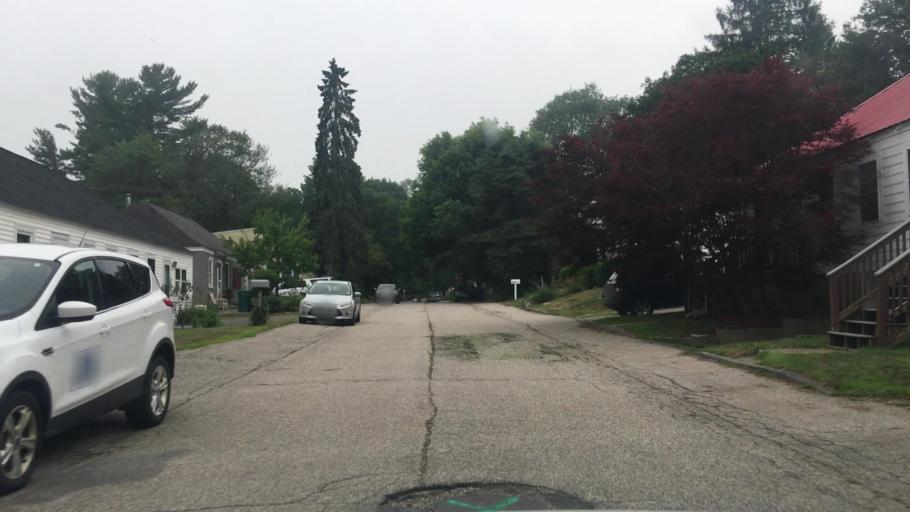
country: US
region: Maine
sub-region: York County
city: Kittery
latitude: 43.0929
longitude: -70.7321
